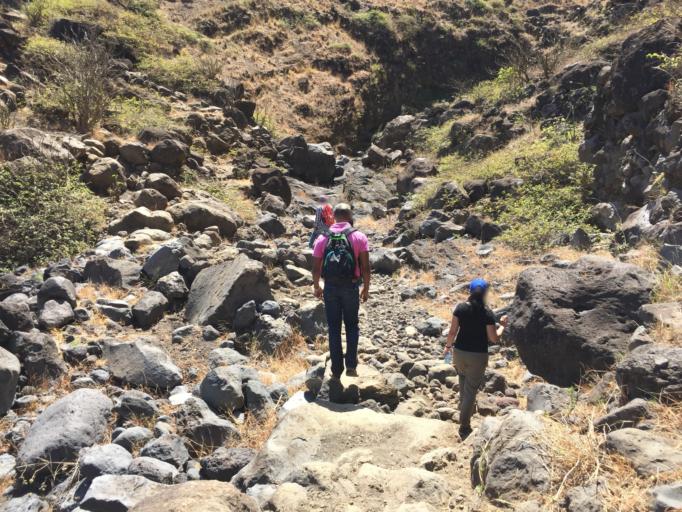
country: CV
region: Mosteiros
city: Porto dos Mosteiros
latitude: 15.0082
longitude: -24.3914
